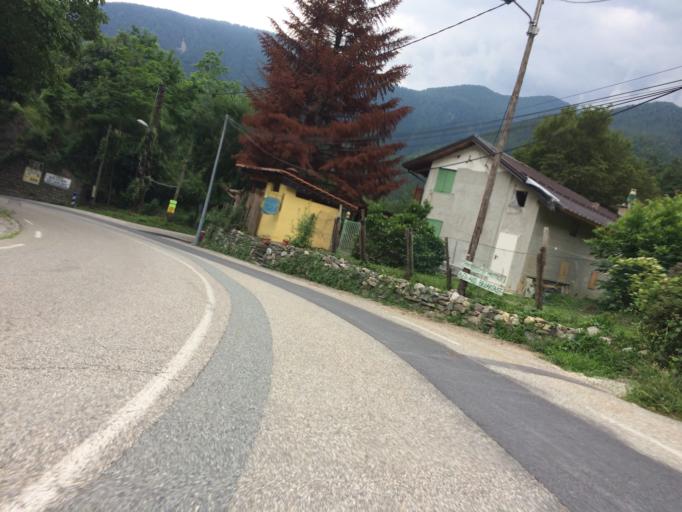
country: FR
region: Provence-Alpes-Cote d'Azur
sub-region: Departement des Alpes-Maritimes
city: Tende
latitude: 44.1151
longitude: 7.5645
